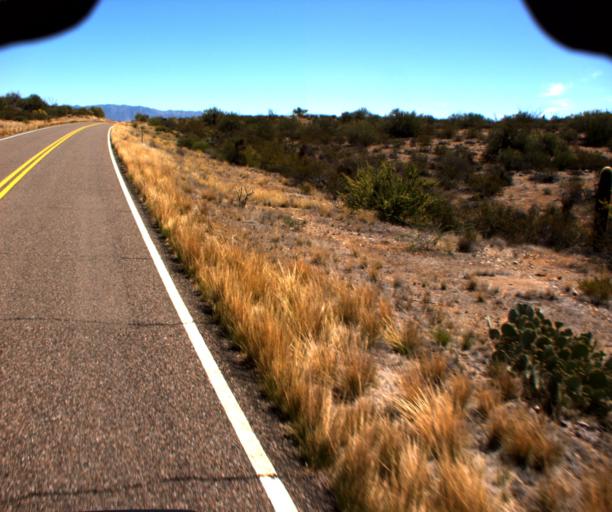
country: US
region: Arizona
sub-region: Yavapai County
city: Congress
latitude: 34.1060
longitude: -112.9927
